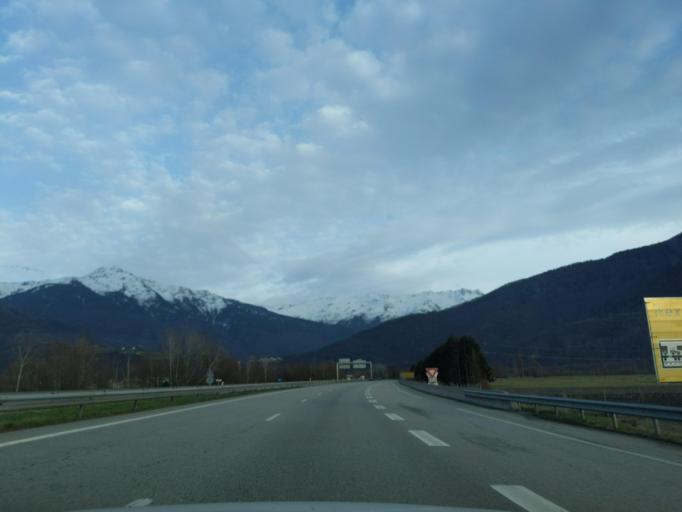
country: FR
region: Rhone-Alpes
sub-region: Departement de la Savoie
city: Aiton
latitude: 45.5651
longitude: 6.2232
